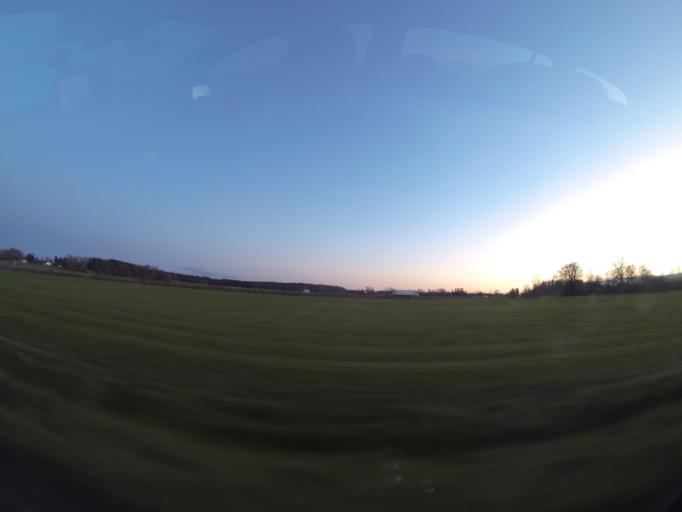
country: SE
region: OErebro
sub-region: Lindesbergs Kommun
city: Fellingsbro
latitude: 59.3313
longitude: 15.5130
